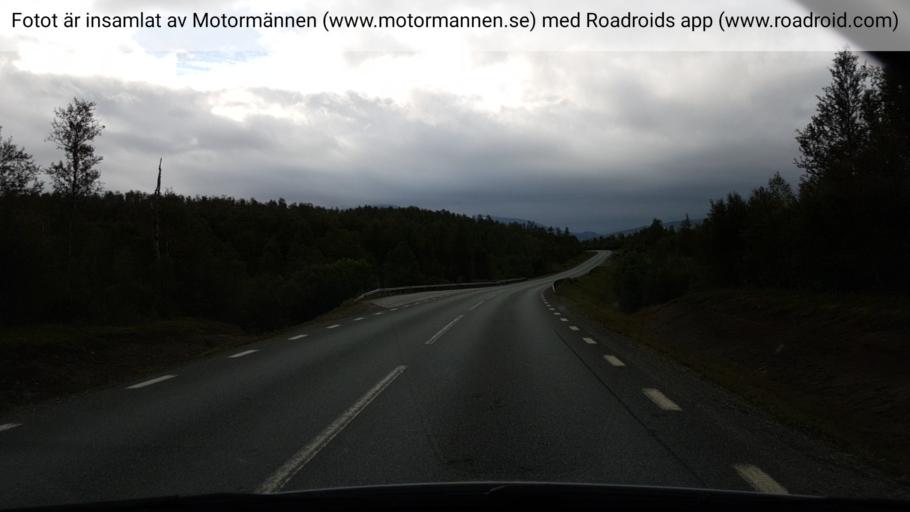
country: NO
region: Nordland
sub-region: Rana
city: Mo i Rana
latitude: 66.0674
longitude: 14.8742
